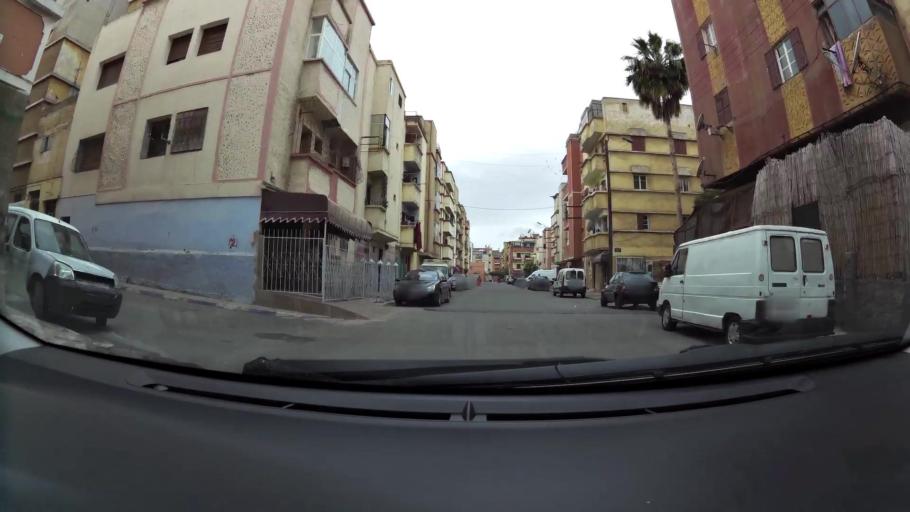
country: MA
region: Grand Casablanca
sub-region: Casablanca
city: Casablanca
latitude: 33.5698
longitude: -7.5555
